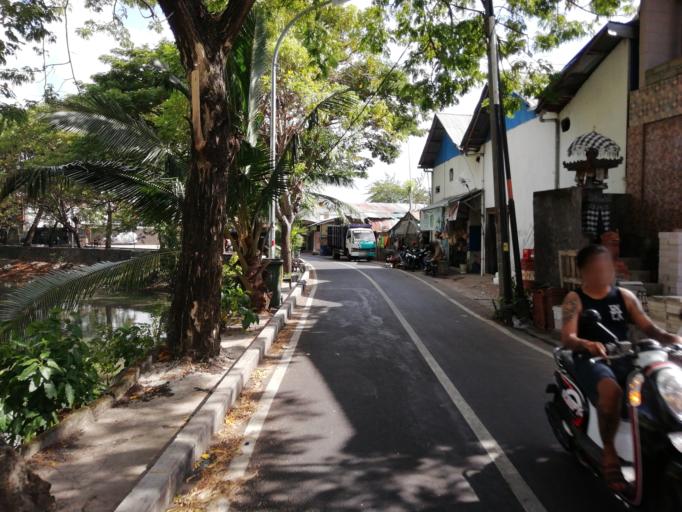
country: ID
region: Bali
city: Kuta
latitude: -8.7084
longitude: 115.1775
